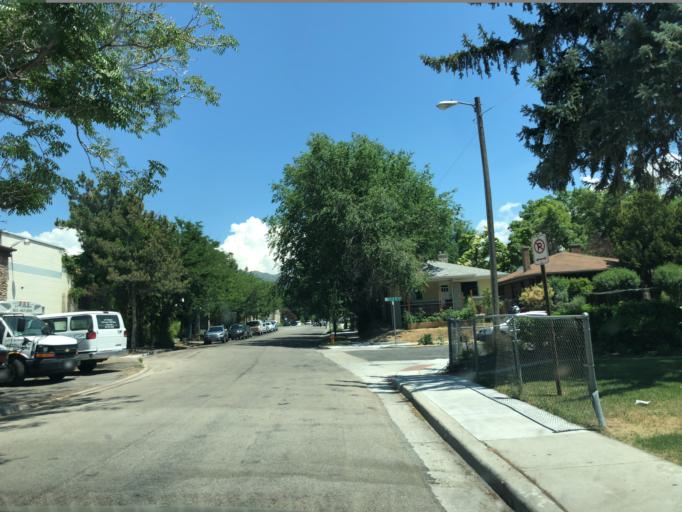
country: US
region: Utah
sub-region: Salt Lake County
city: South Salt Lake
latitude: 40.7221
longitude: -111.8730
